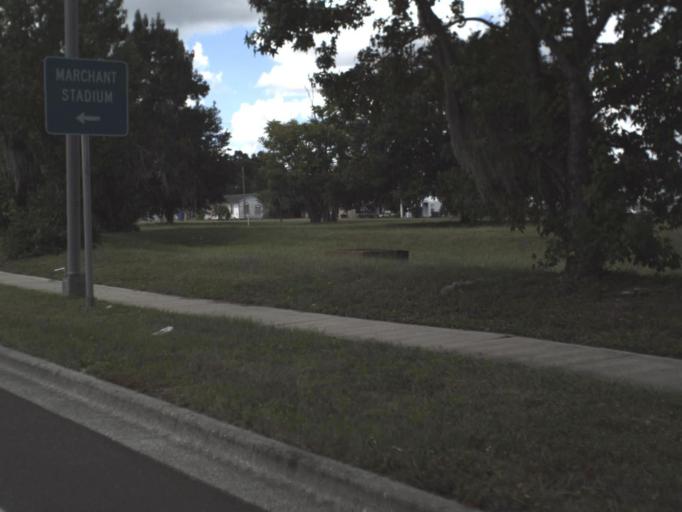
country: US
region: Florida
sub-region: Polk County
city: Lakeland
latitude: 28.0638
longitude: -81.9574
